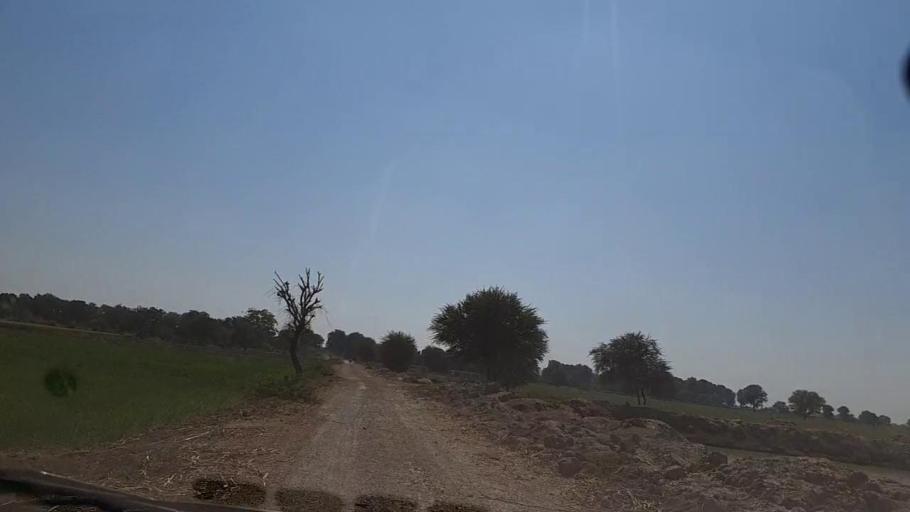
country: PK
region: Sindh
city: Mirpur Khas
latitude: 25.4286
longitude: 69.0559
